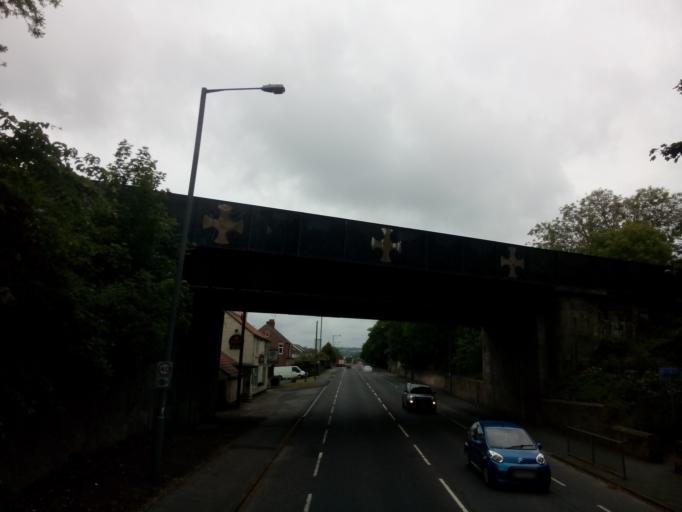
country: GB
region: England
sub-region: County Durham
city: Chester-le-Street
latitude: 54.8750
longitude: -1.5756
